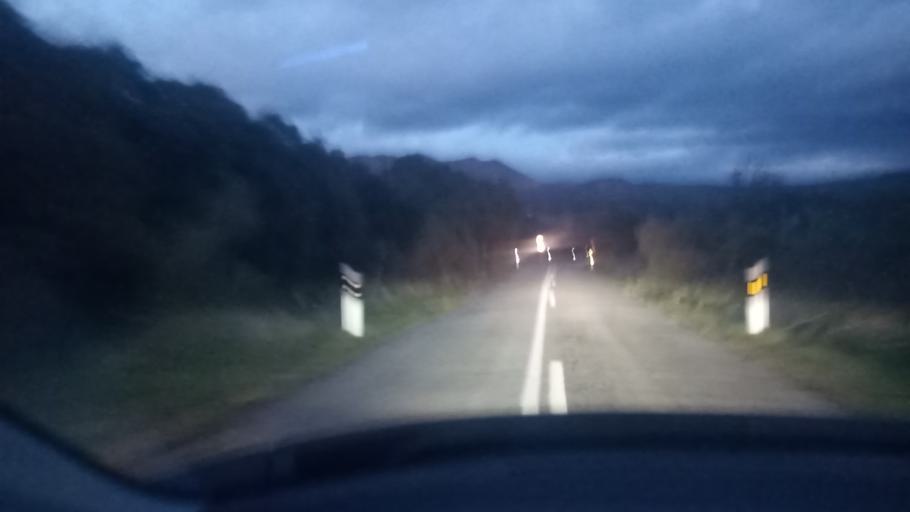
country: ES
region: Madrid
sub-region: Provincia de Madrid
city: Colmenar del Arroyo
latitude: 40.4410
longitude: -4.2411
